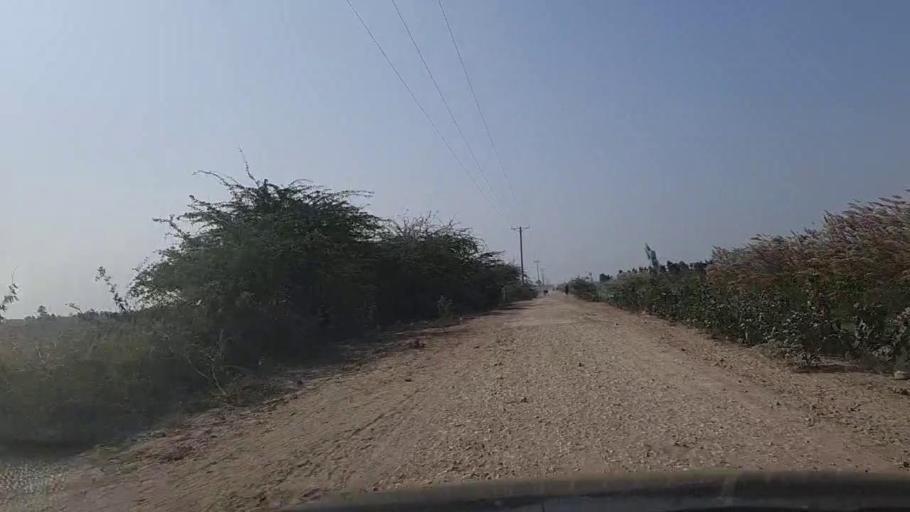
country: PK
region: Sindh
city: Gharo
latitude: 24.6857
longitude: 67.6033
